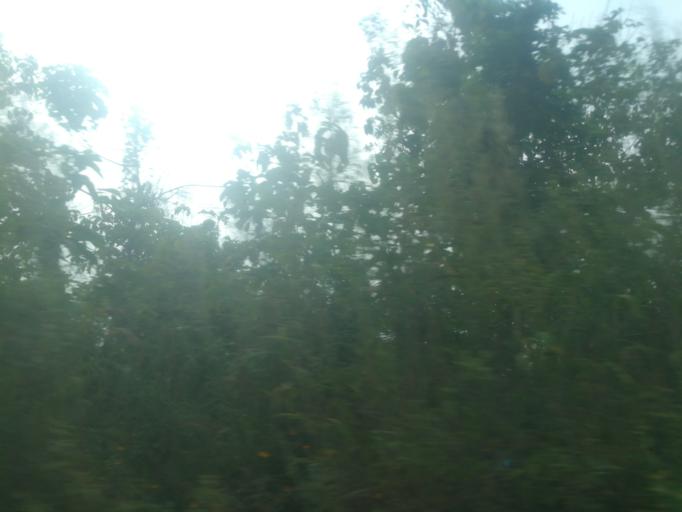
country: NG
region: Ogun
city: Ayetoro
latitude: 7.3246
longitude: 3.0683
